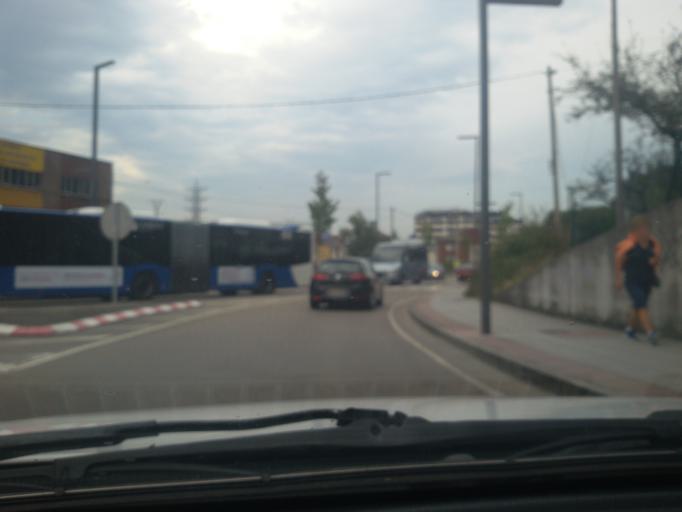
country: ES
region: Asturias
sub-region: Province of Asturias
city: Lugones
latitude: 43.3977
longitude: -5.8134
